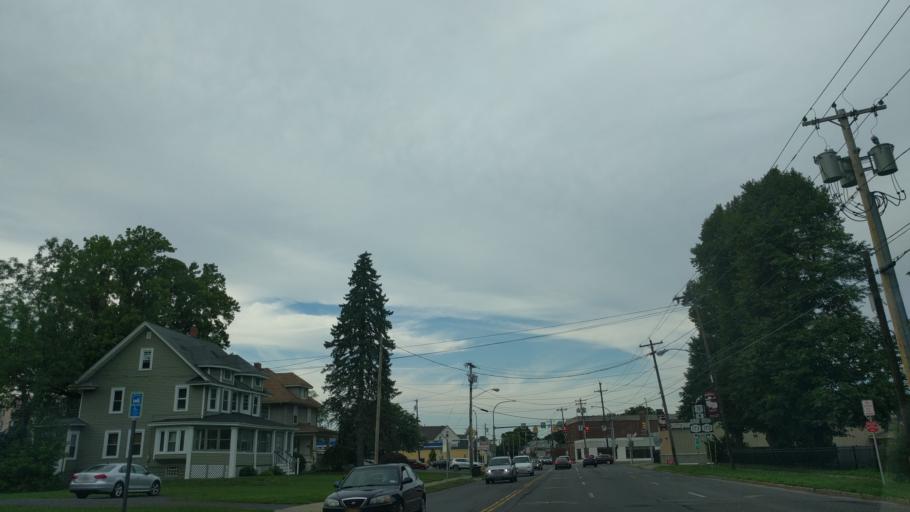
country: US
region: New York
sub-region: Onondaga County
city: Nedrow
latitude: 42.9996
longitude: -76.1428
